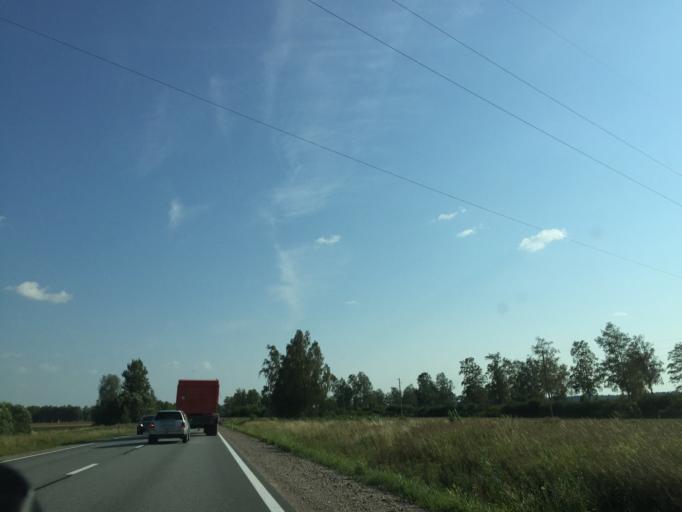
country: LT
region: Siauliu apskritis
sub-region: Joniskis
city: Joniskis
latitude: 56.4321
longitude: 23.6866
